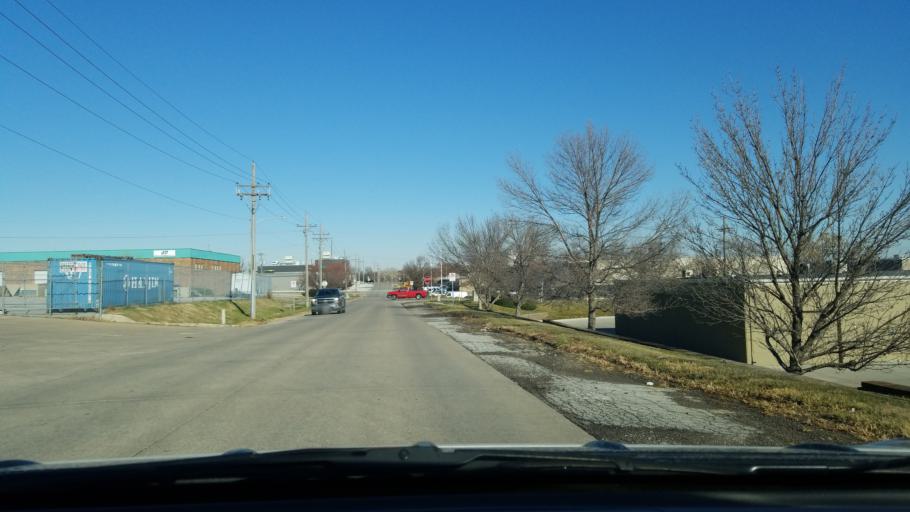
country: US
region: Nebraska
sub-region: Douglas County
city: Ralston
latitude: 41.2133
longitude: -96.0719
